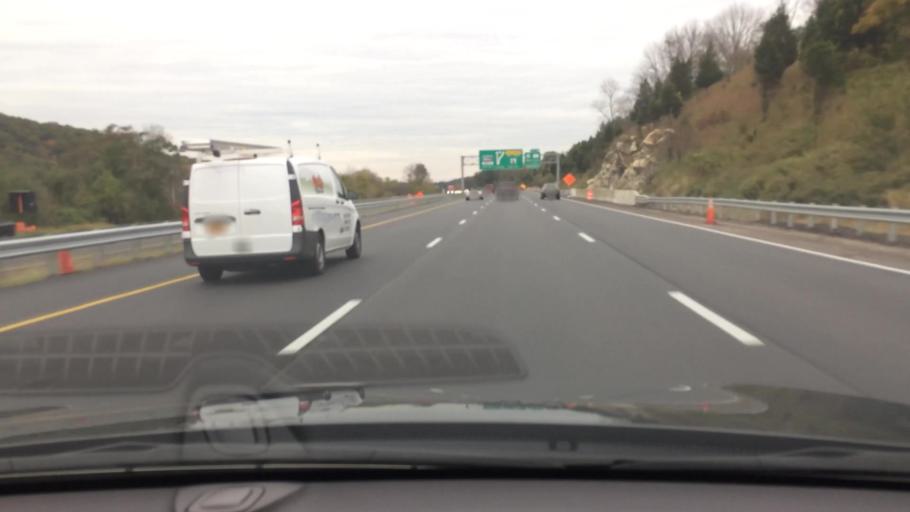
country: US
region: New York
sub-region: Orange County
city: Harriman
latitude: 41.2793
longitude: -74.1459
